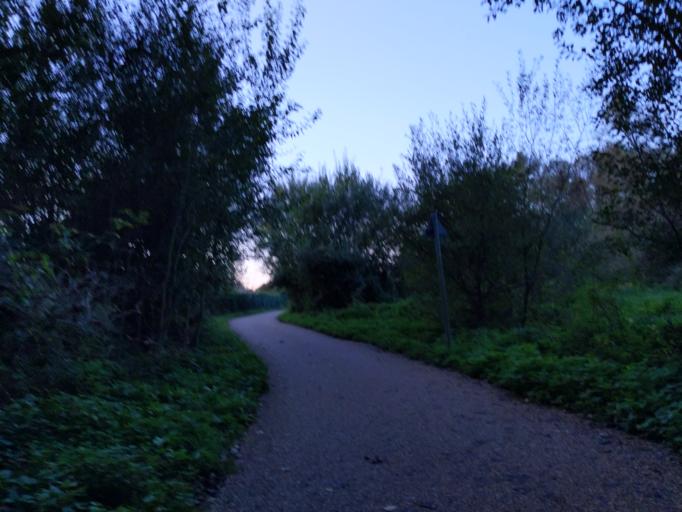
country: GB
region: England
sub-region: Oxfordshire
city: Radley
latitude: 51.7184
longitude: -1.2427
